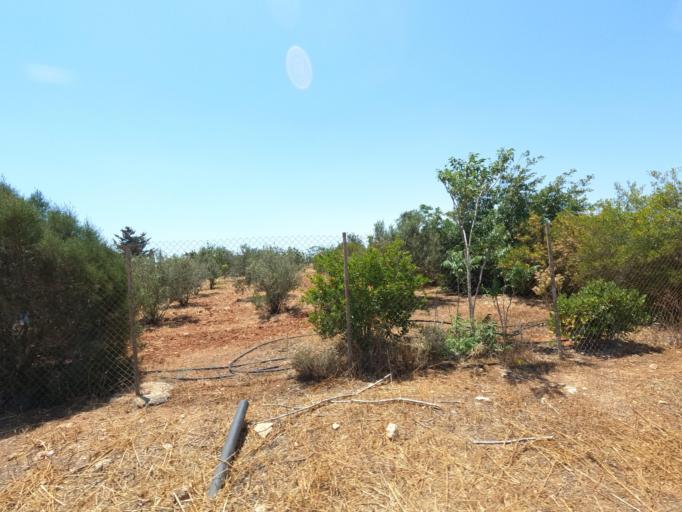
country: CY
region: Larnaka
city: Xylotymbou
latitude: 35.0204
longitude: 33.7195
